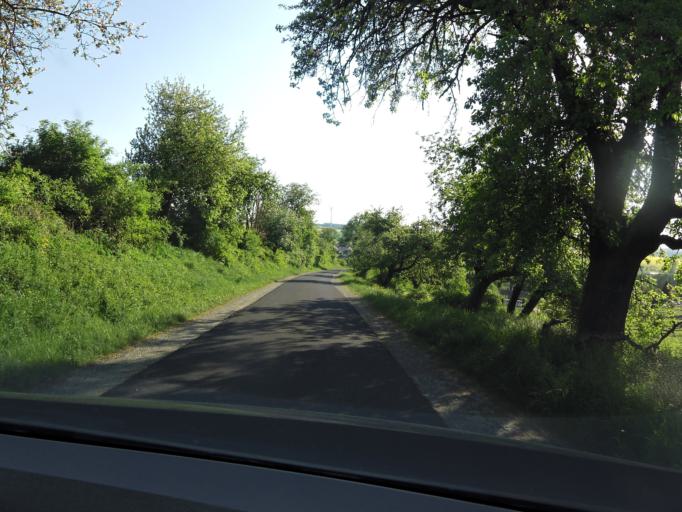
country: DE
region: Thuringia
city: Lauterbach
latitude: 51.0727
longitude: 10.3546
